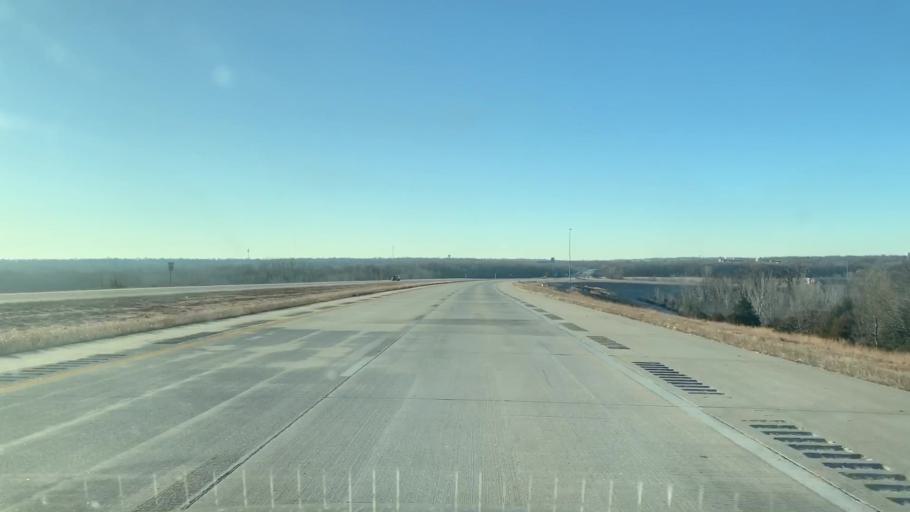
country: US
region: Kansas
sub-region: Bourbon County
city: Fort Scott
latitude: 37.8621
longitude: -94.7032
